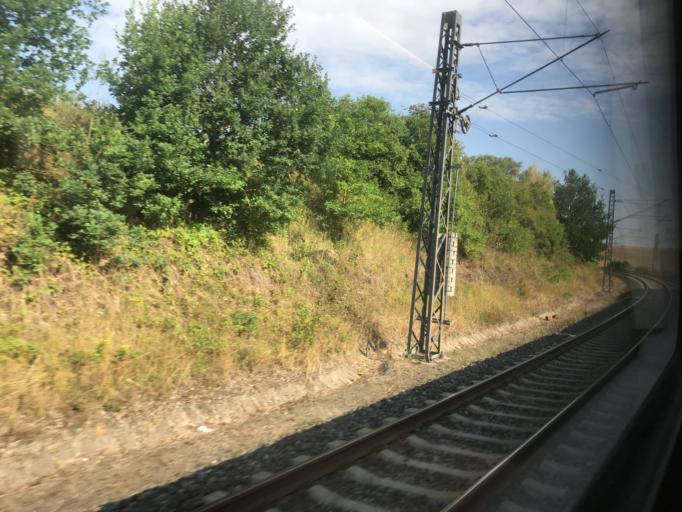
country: CZ
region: Central Bohemia
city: Bystrice
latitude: 49.7478
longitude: 14.6784
